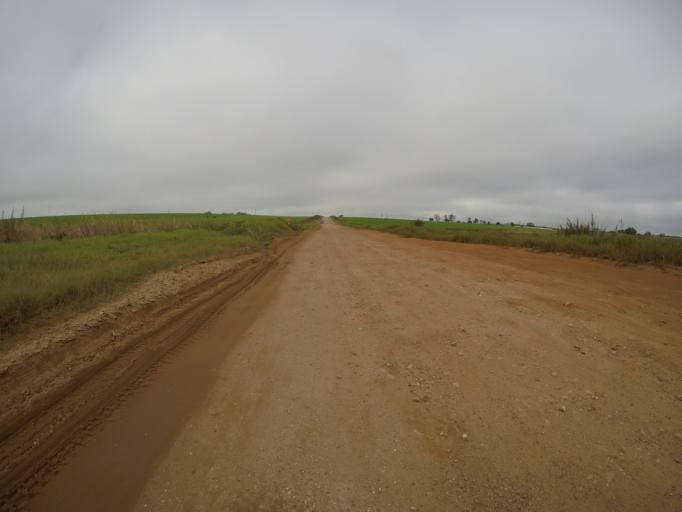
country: ZA
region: Eastern Cape
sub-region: Cacadu District Municipality
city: Kareedouw
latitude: -34.0274
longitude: 24.2425
